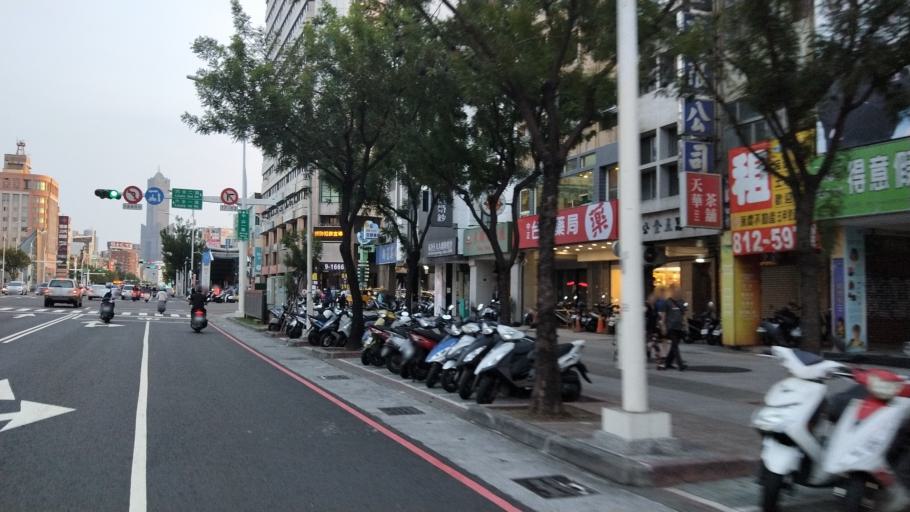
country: TW
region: Kaohsiung
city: Kaohsiung
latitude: 22.6336
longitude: 120.3020
